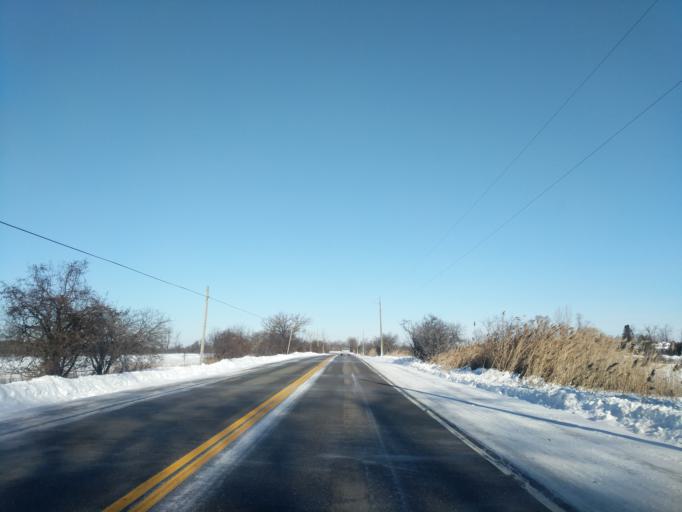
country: CA
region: Ontario
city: Pickering
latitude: 43.8623
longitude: -79.1341
